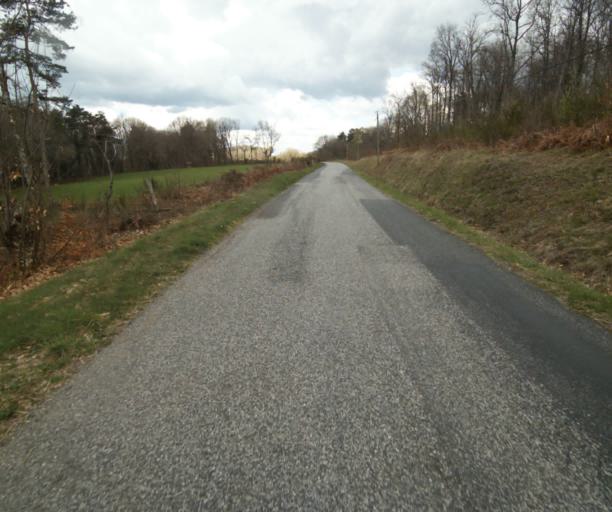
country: FR
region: Limousin
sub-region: Departement de la Correze
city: Correze
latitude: 45.2667
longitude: 1.8994
